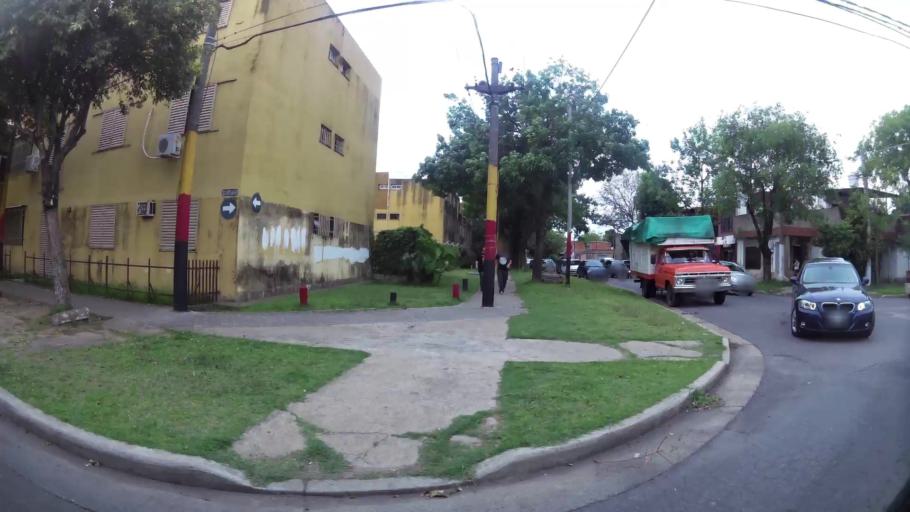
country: AR
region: Santa Fe
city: Gobernador Galvez
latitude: -32.9946
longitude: -60.6681
